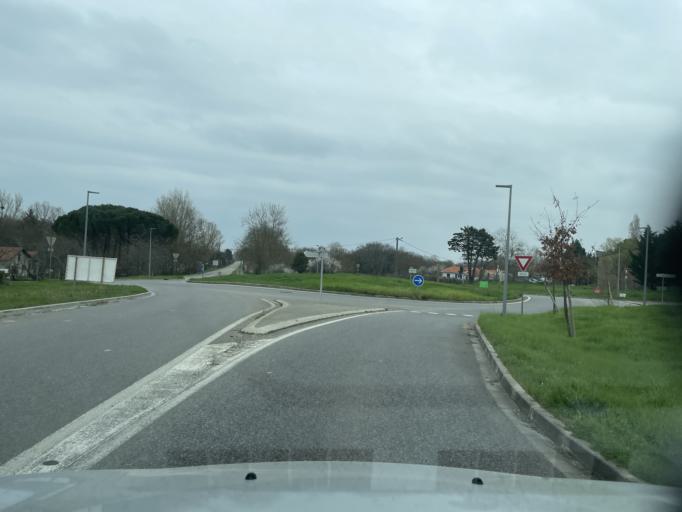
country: FR
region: Midi-Pyrenees
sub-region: Departement du Gers
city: Pujaudran
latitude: 43.5913
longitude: 1.1762
